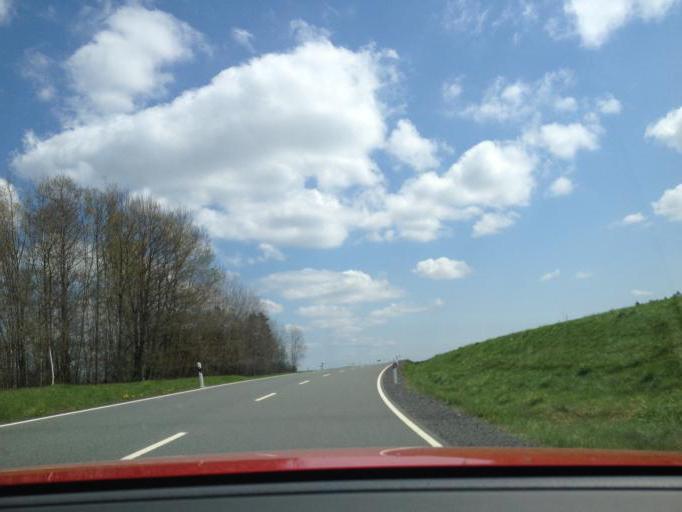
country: DE
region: Bavaria
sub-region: Upper Franconia
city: Marktredwitz
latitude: 49.9775
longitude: 12.1040
